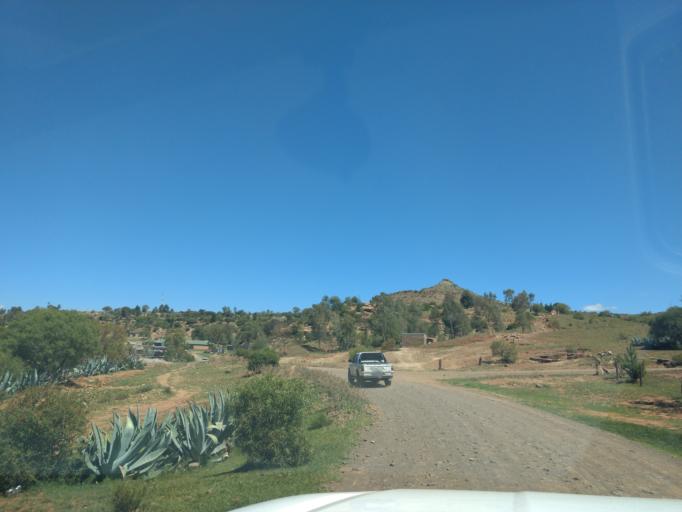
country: LS
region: Maseru
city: Maseru
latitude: -29.4901
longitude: 27.3705
